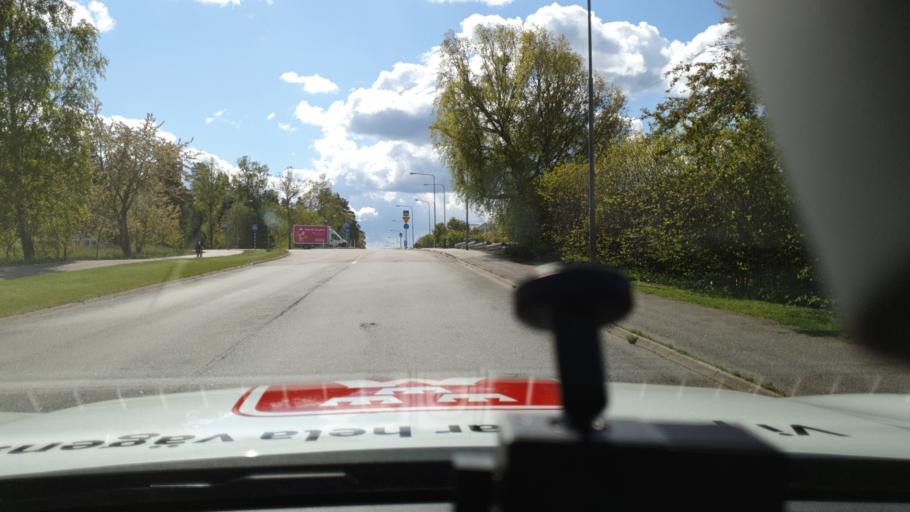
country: SE
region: Kalmar
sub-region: Vimmerby Kommun
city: Vimmerby
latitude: 57.6763
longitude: 15.8664
